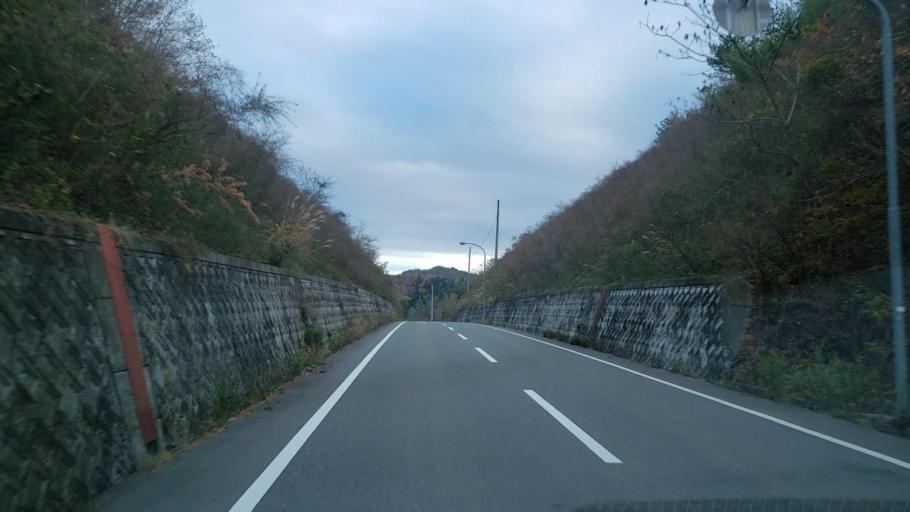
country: JP
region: Tokushima
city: Wakimachi
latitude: 34.1818
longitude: 134.1804
